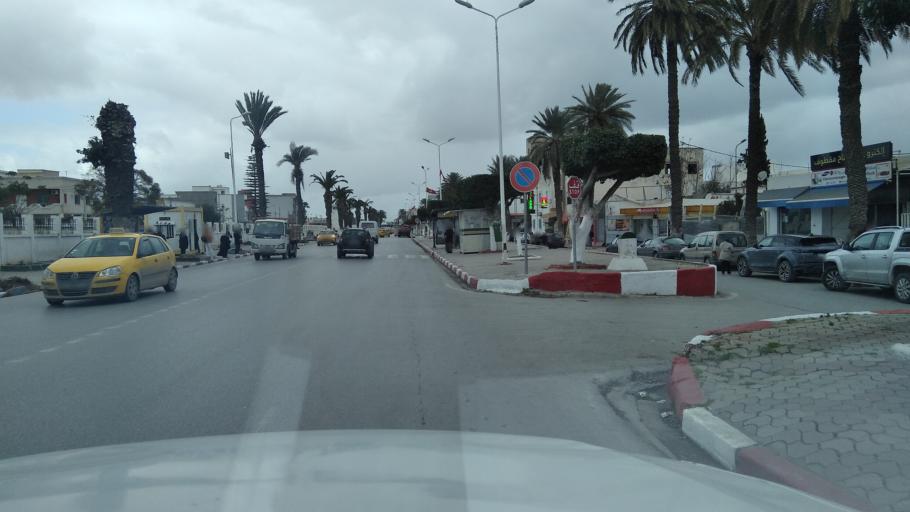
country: TN
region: Bin 'Arus
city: Ben Arous
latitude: 36.7531
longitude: 10.2232
